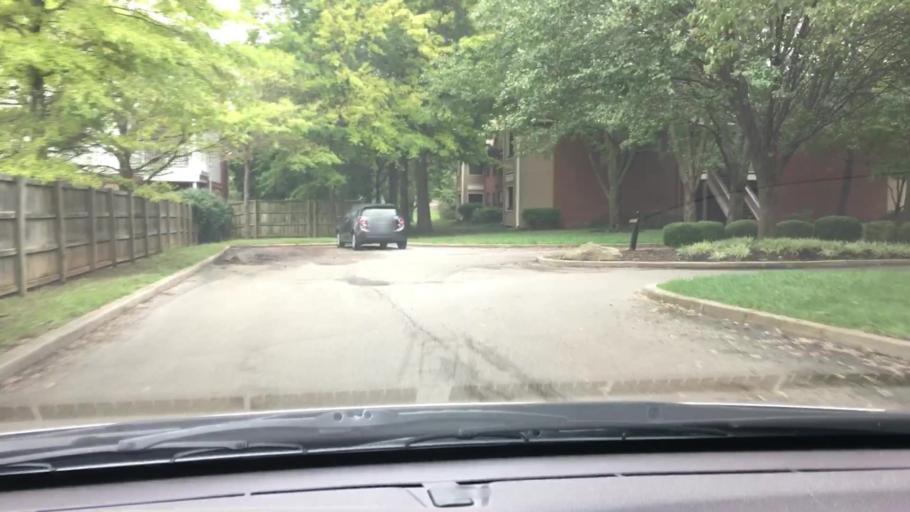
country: US
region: Kentucky
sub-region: Jefferson County
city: Beechwood Village
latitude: 38.2409
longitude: -85.6286
